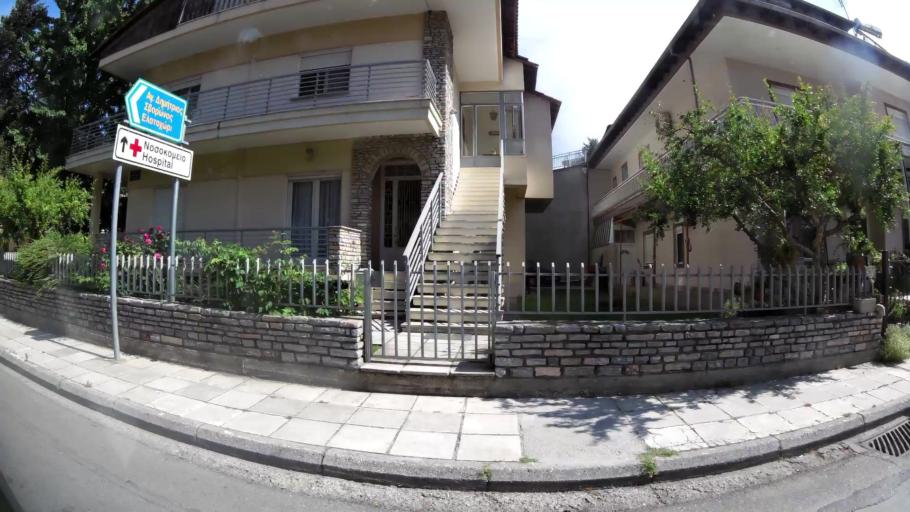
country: GR
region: Central Macedonia
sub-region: Nomos Pierias
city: Katerini
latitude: 40.2801
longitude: 22.4982
